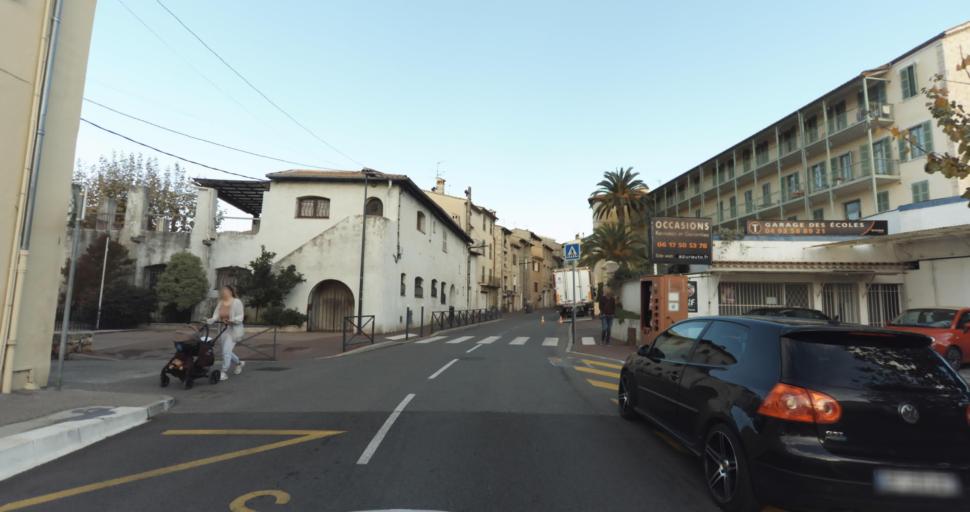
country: FR
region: Provence-Alpes-Cote d'Azur
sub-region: Departement des Alpes-Maritimes
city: Vence
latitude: 43.7209
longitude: 7.1154
